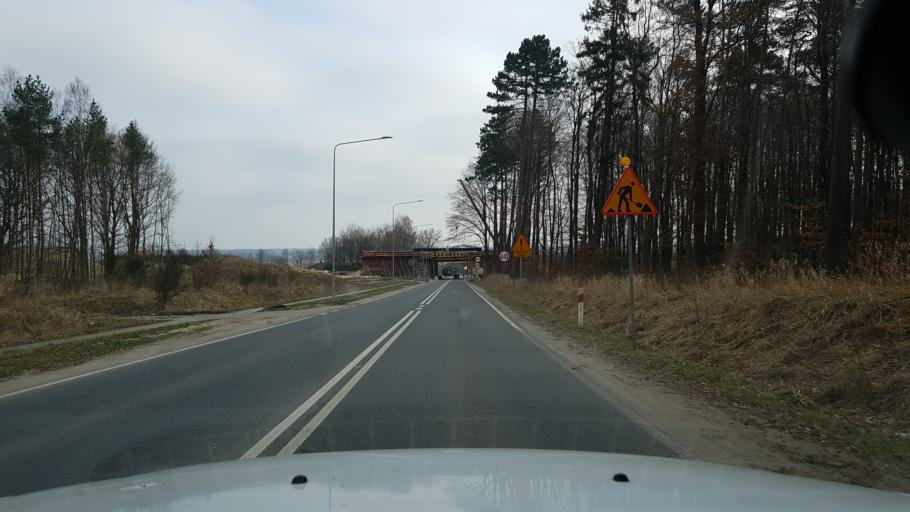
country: PL
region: West Pomeranian Voivodeship
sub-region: Powiat koszalinski
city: Sianow
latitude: 54.2241
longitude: 16.2451
